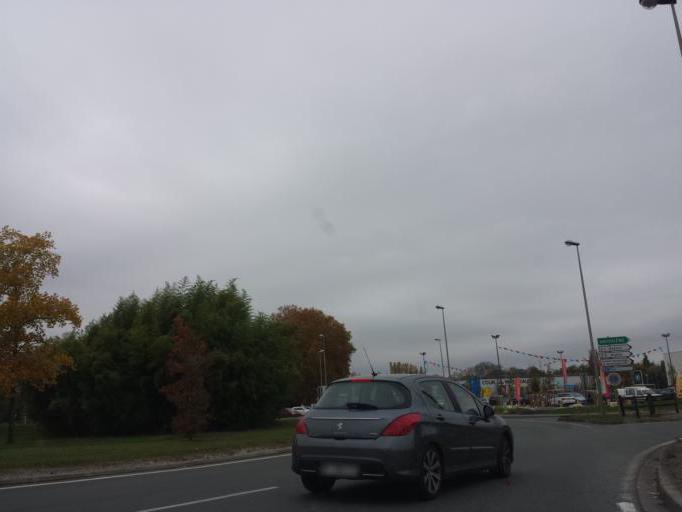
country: FR
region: Poitou-Charentes
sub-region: Departement de la Charente
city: Angouleme
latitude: 45.6352
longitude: 0.1257
